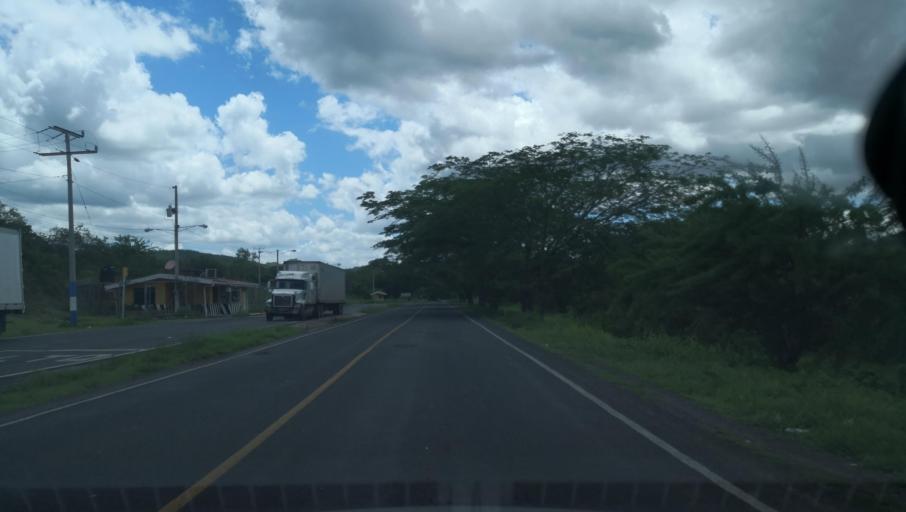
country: NI
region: Madriz
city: Palacaguina
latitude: 13.4331
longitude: -86.4120
